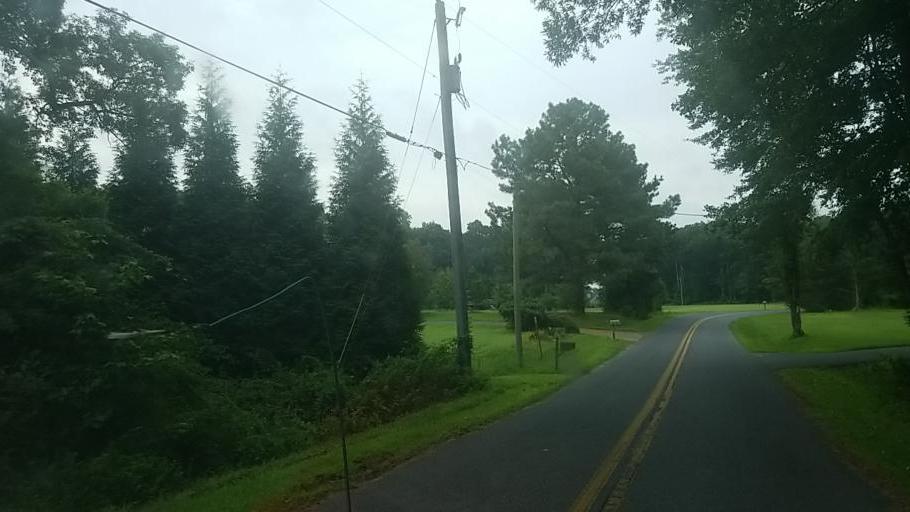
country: US
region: Maryland
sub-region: Worcester County
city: Ocean Pines
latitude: 38.4235
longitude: -75.1913
